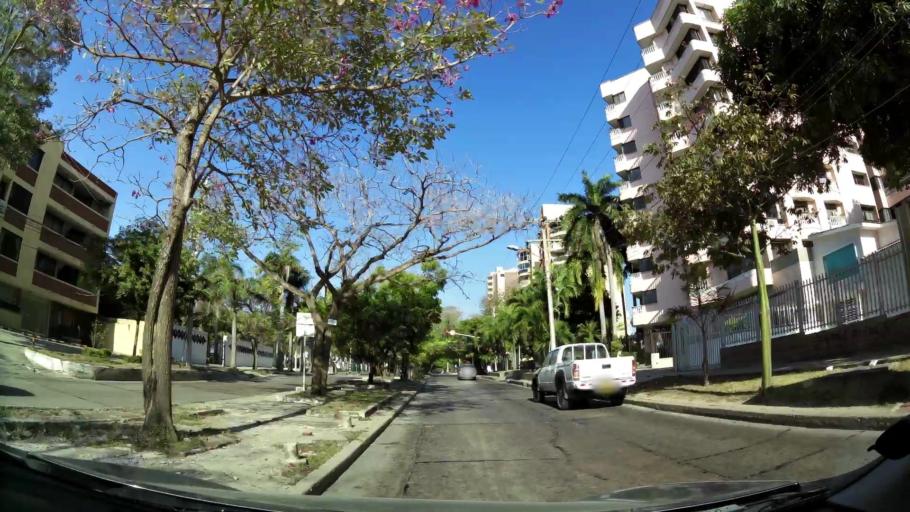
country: CO
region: Atlantico
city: Barranquilla
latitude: 10.9970
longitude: -74.7970
